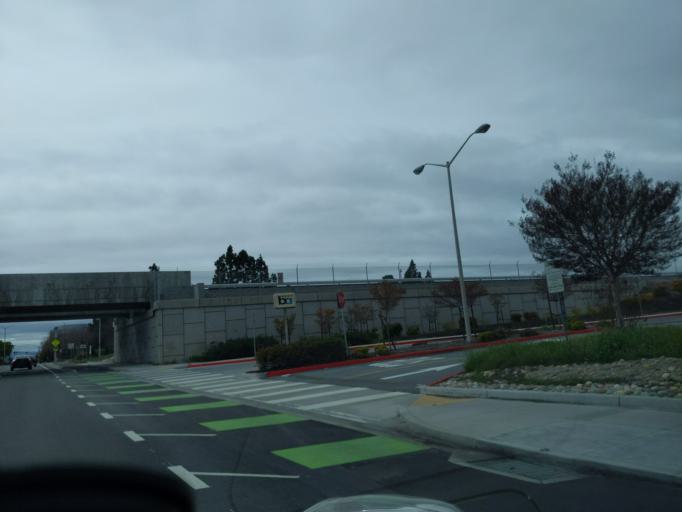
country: US
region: California
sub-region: Alameda County
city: Fremont
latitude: 37.5565
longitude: -121.9745
